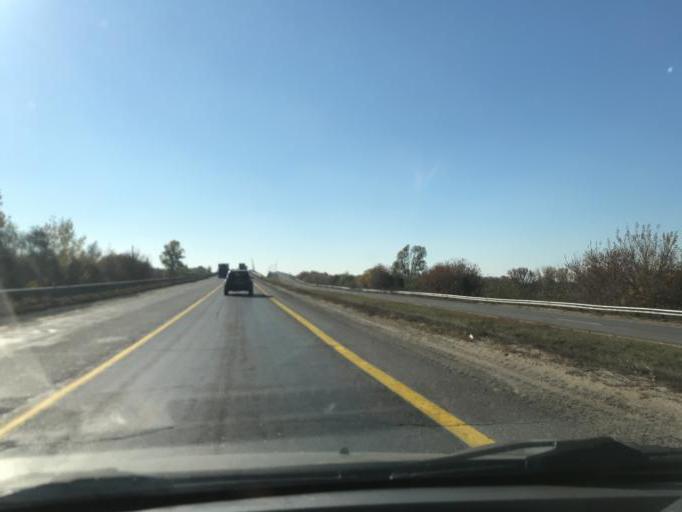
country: BY
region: Gomel
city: Horad Rechytsa
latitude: 52.3273
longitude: 30.5341
